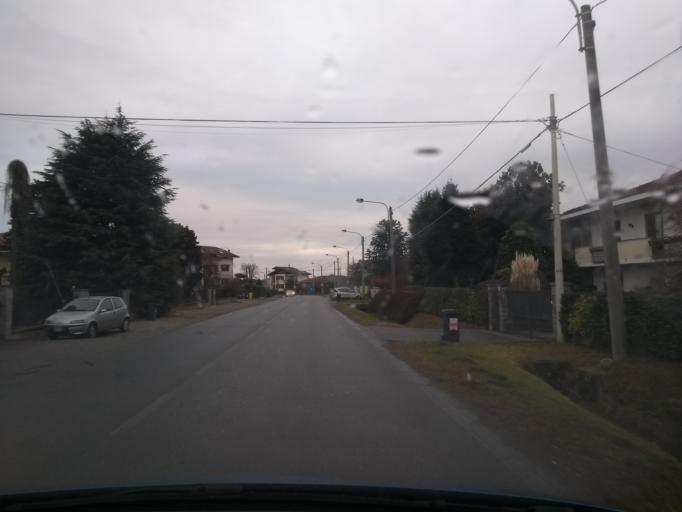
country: IT
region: Piedmont
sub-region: Provincia di Torino
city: Castellamonte
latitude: 45.3769
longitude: 7.7109
